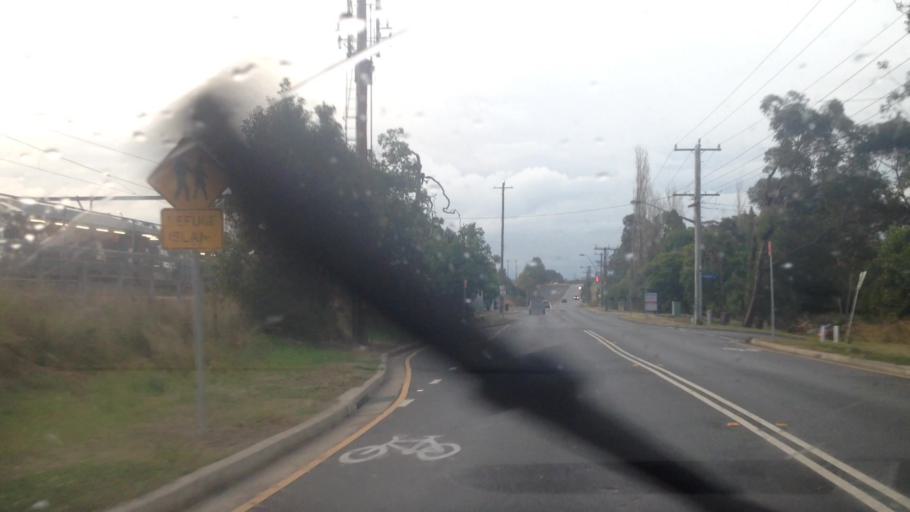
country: AU
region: New South Wales
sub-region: Wyong Shire
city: Charmhaven
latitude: -33.1810
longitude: 151.4874
